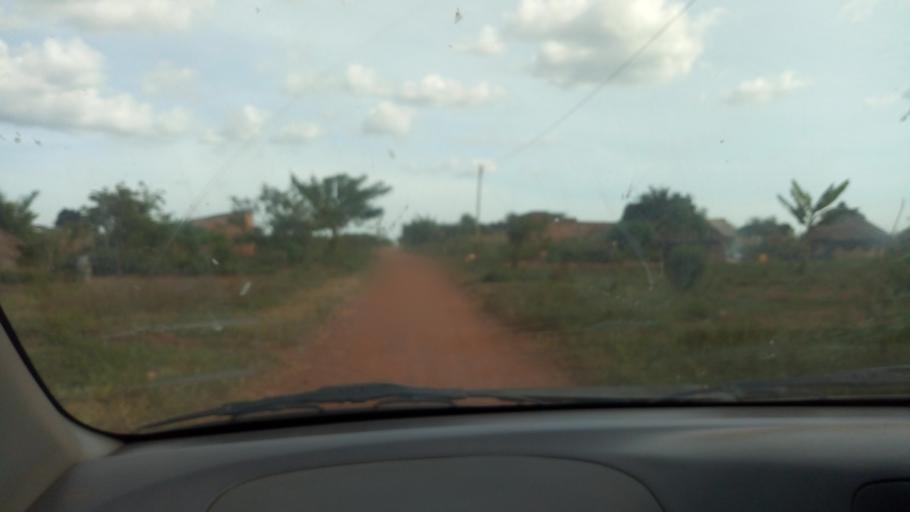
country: UG
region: Western Region
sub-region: Kiryandongo District
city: Kiryandongo
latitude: 1.8091
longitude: 31.9432
